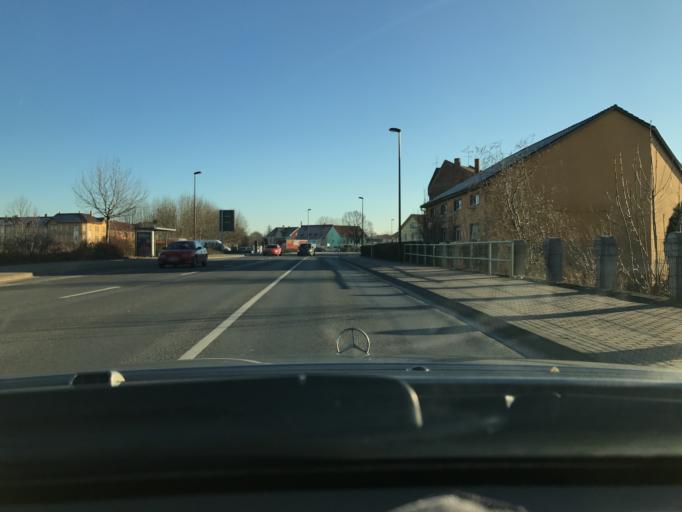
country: DE
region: Thuringia
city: Muehlhausen
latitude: 51.2152
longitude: 10.4659
